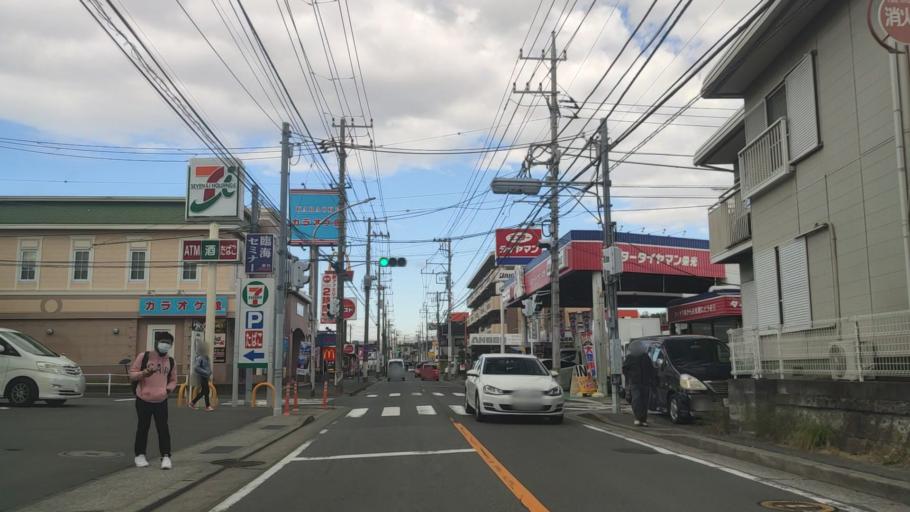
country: JP
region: Kanagawa
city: Minami-rinkan
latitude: 35.4232
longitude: 139.5319
